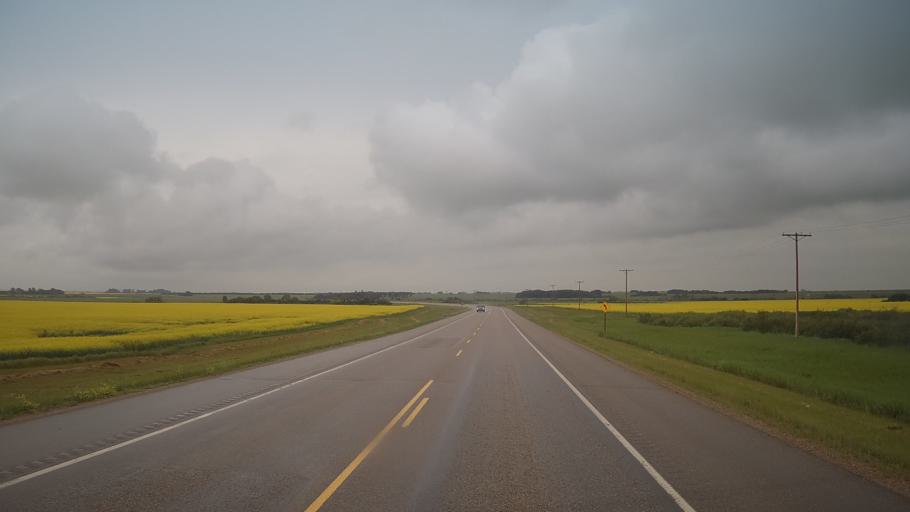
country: CA
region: Saskatchewan
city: Wilkie
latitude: 52.4319
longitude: -108.9222
